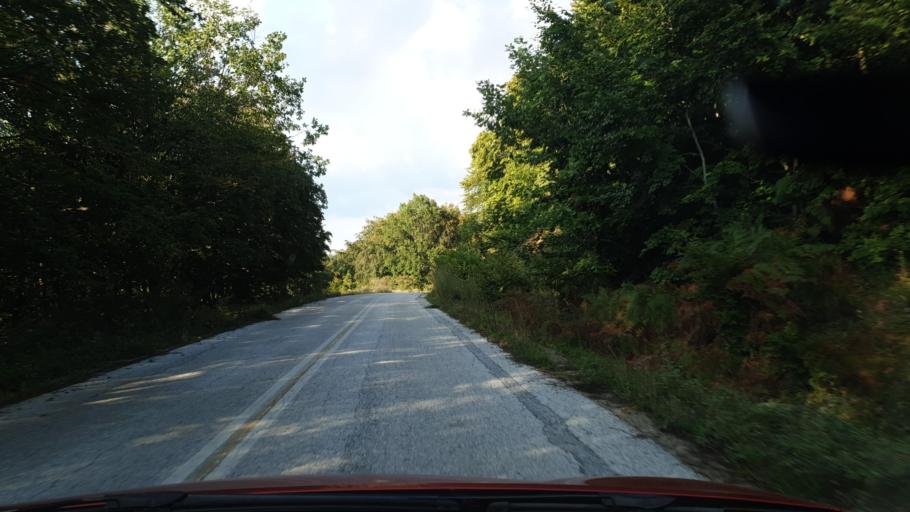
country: GR
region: Central Macedonia
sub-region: Nomos Chalkidikis
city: Galatista
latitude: 40.5056
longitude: 23.2415
